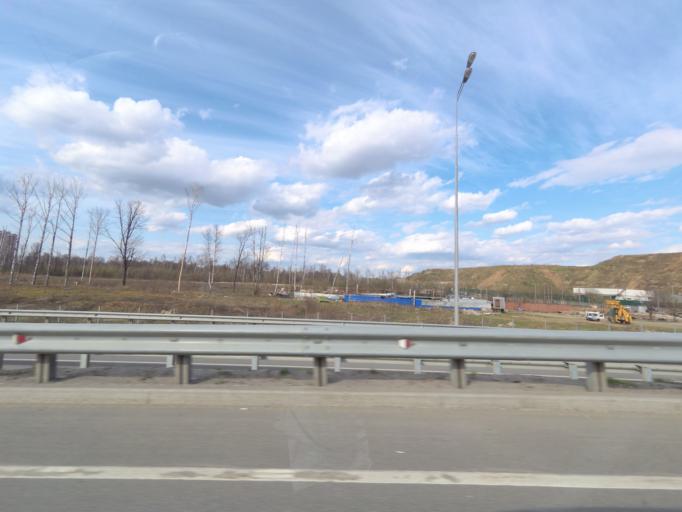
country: RU
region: Moscow
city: Businovo
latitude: 55.8954
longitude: 37.4941
